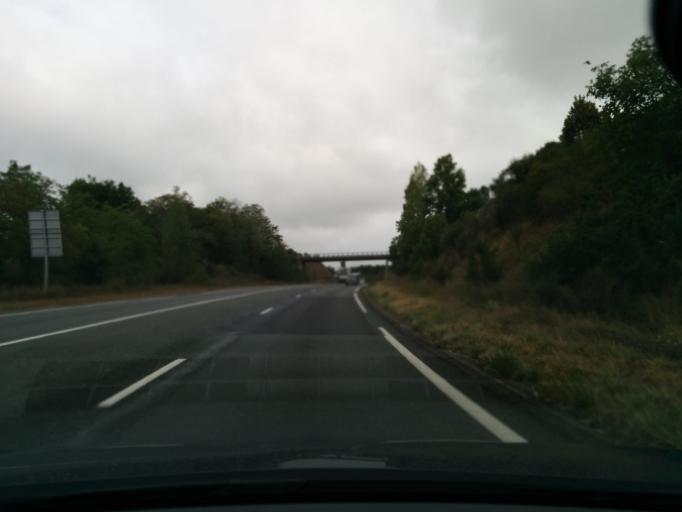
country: FR
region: Midi-Pyrenees
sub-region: Departement du Lot
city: Cahors
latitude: 44.4354
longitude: 1.4261
